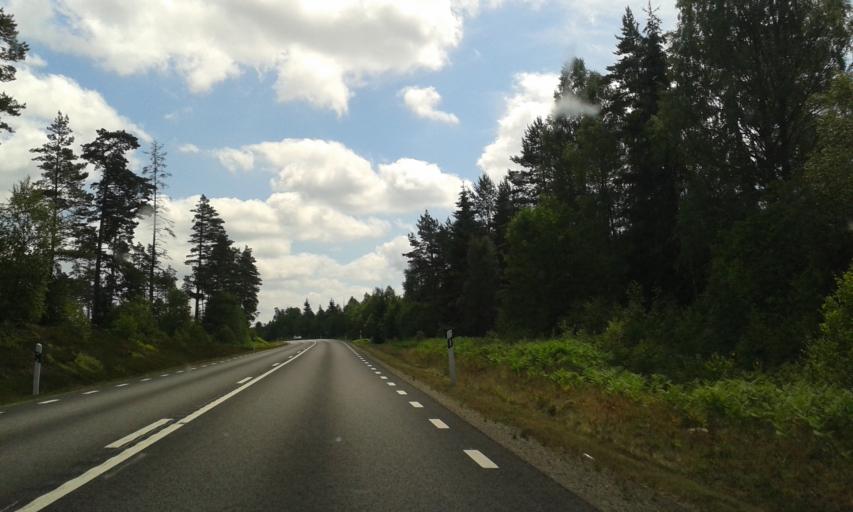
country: SE
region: Joenkoeping
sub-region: Varnamo Kommun
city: Rydaholm
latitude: 56.9303
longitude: 14.4002
